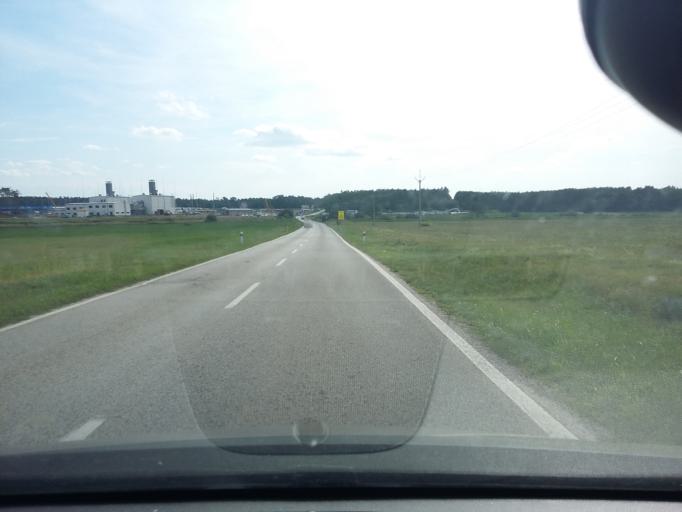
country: SK
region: Trnavsky
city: Gbely
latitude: 48.6006
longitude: 17.1963
